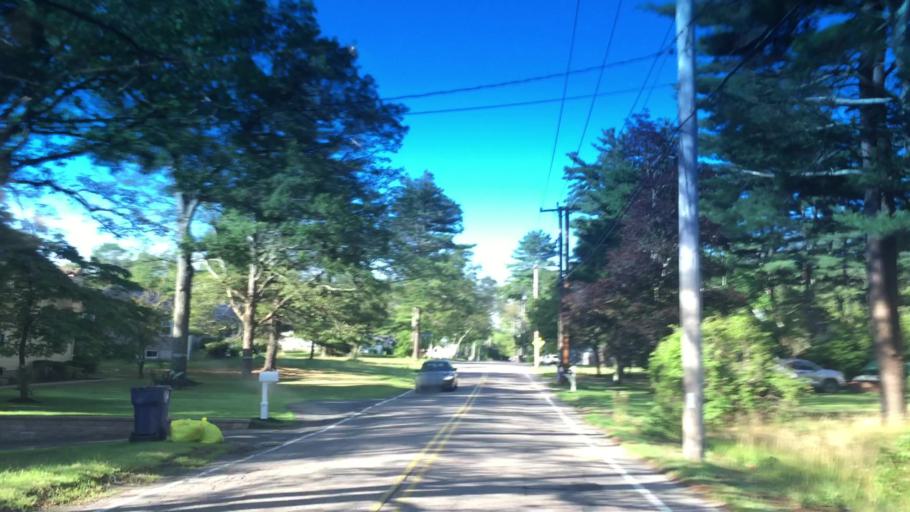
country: US
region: Massachusetts
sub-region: Norfolk County
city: Medway
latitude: 42.1557
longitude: -71.3904
